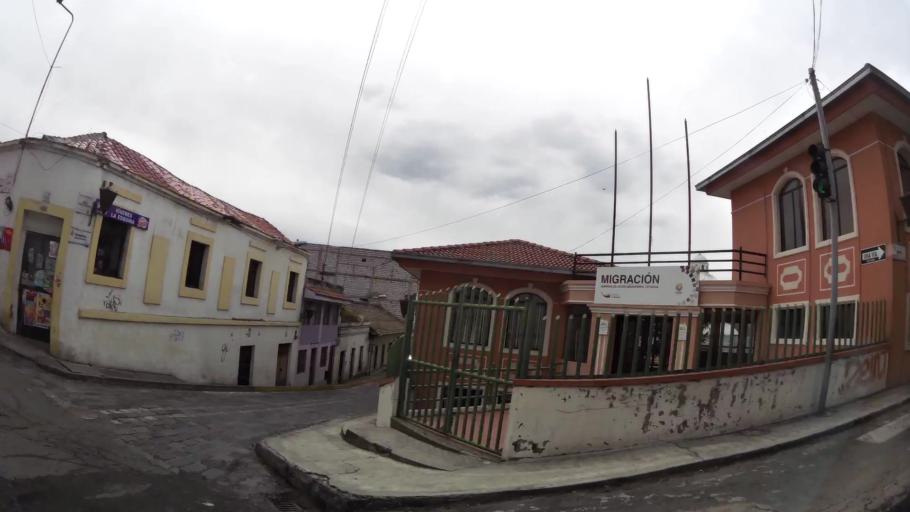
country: EC
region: Cotopaxi
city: Latacunga
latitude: -0.9334
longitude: -78.6124
